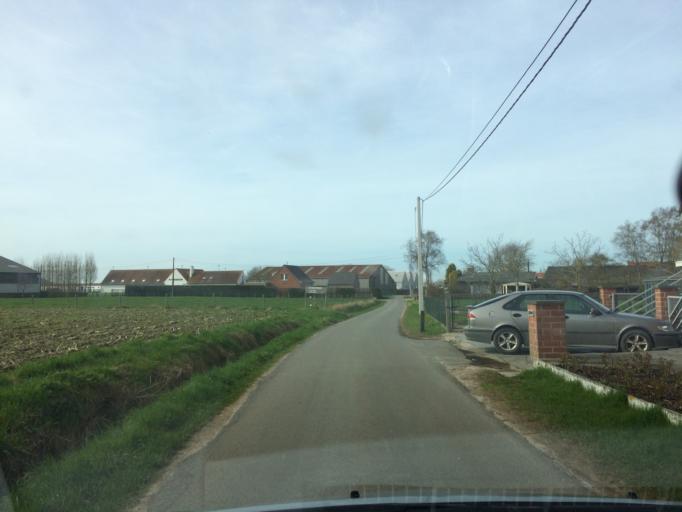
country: BE
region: Flanders
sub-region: Provincie West-Vlaanderen
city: Diksmuide
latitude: 50.9949
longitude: 2.8643
